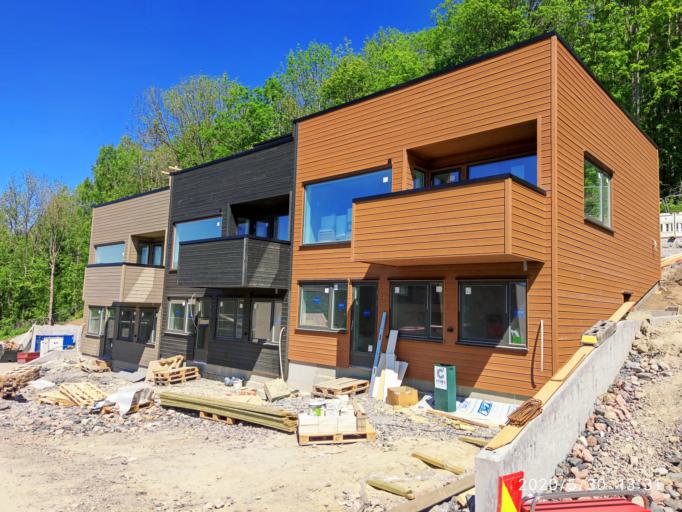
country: NO
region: Buskerud
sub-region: Lier
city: Tranby
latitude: 59.7915
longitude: 10.2668
